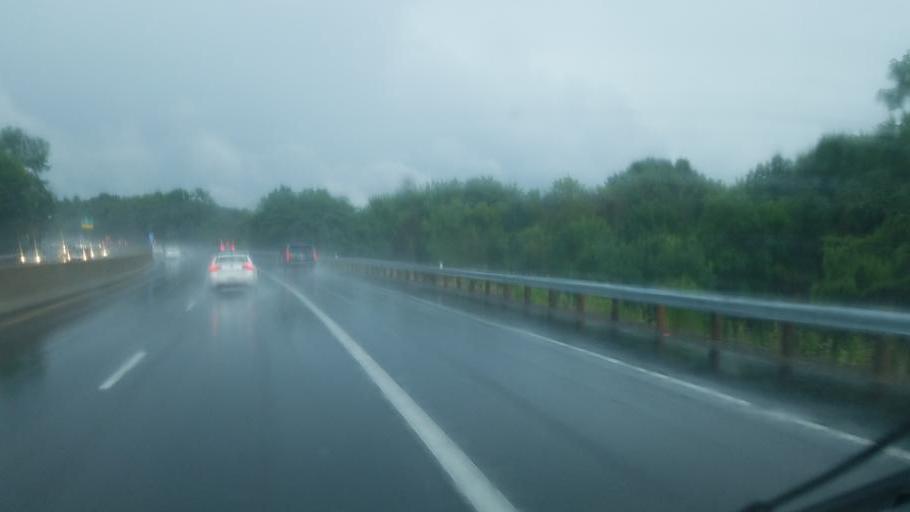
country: US
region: Ohio
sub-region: Trumbull County
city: Howland Center
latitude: 41.2308
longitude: -80.7458
